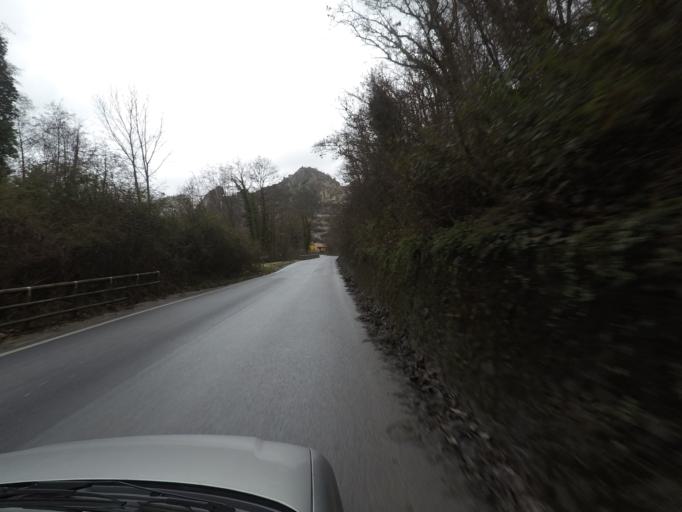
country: IT
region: Tuscany
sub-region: Provincia di Massa-Carrara
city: Massa
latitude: 44.0766
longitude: 10.1323
